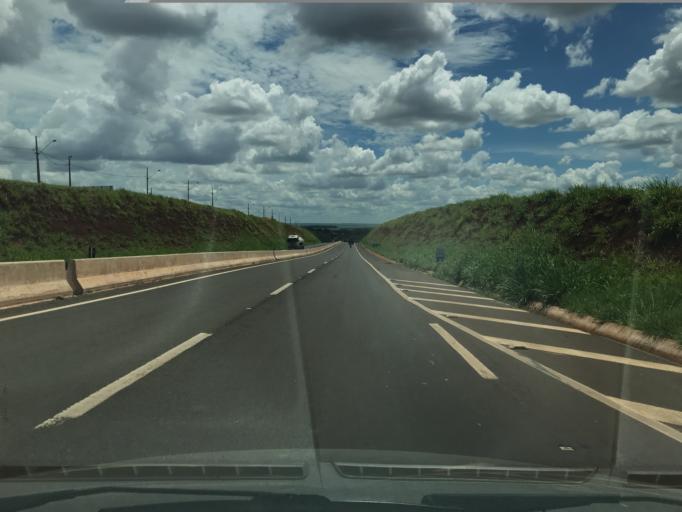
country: BR
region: Parana
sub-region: Maringa
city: Maringa
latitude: -23.3770
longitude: -51.9168
